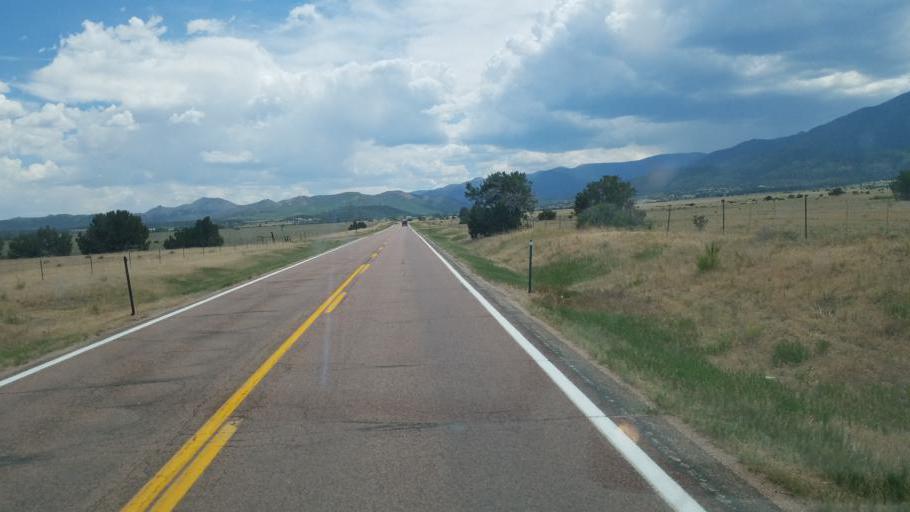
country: US
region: Colorado
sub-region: Fremont County
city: Florence
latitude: 38.2663
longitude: -105.0875
